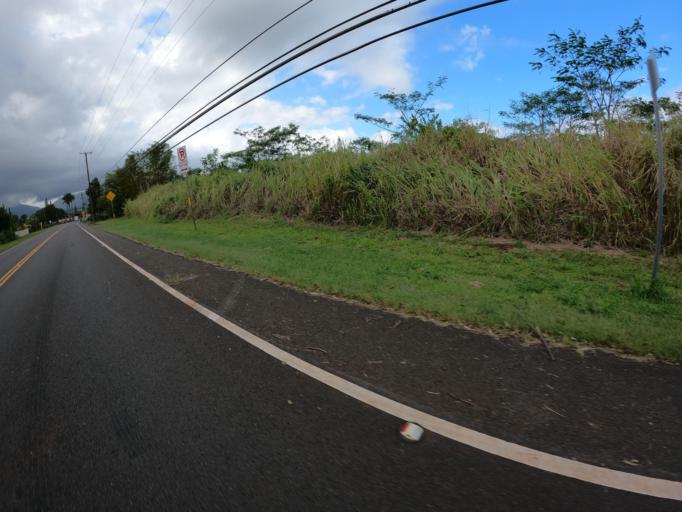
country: US
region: Hawaii
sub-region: Honolulu County
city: Whitmore Village
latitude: 21.5118
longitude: -158.0171
